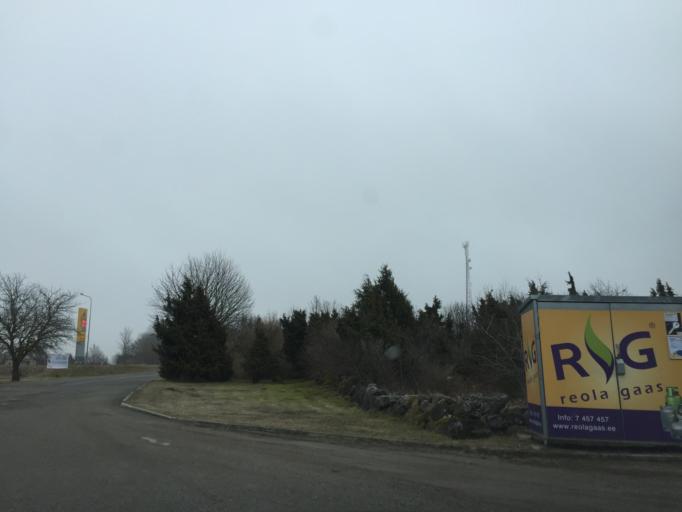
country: EE
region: Laeaene
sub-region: Lihula vald
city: Lihula
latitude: 58.5876
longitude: 23.5276
